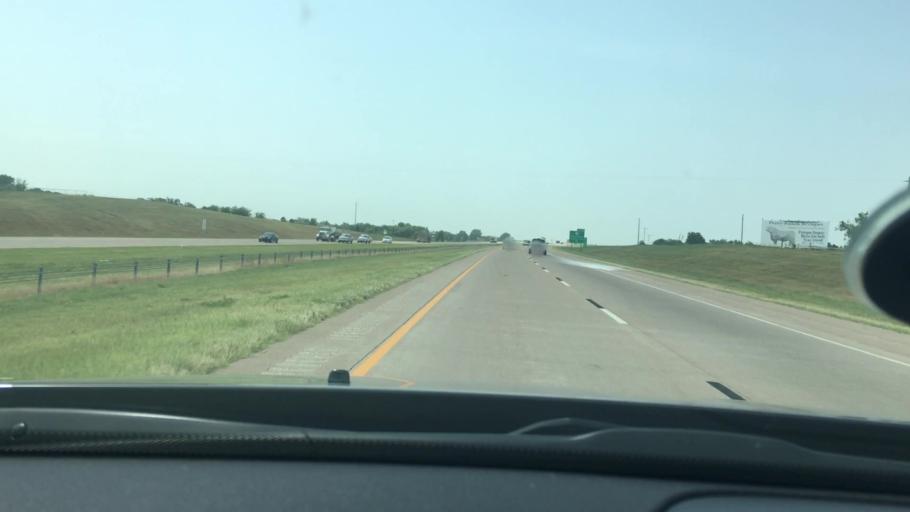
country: US
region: Oklahoma
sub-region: Garvin County
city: Wynnewood
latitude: 34.6606
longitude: -97.2218
